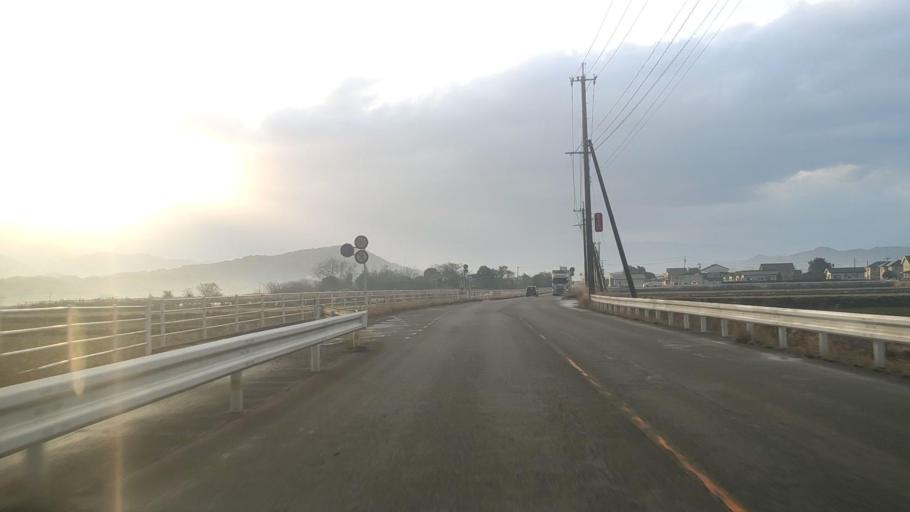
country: JP
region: Kumamoto
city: Uto
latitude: 32.7188
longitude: 130.7712
